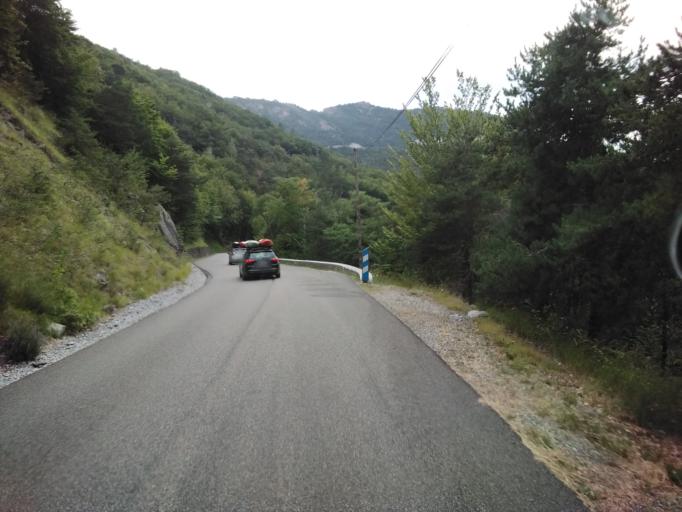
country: FR
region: Provence-Alpes-Cote d'Azur
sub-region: Departement des Alpes-de-Haute-Provence
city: Seyne-les-Alpes
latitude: 44.4489
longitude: 6.4002
